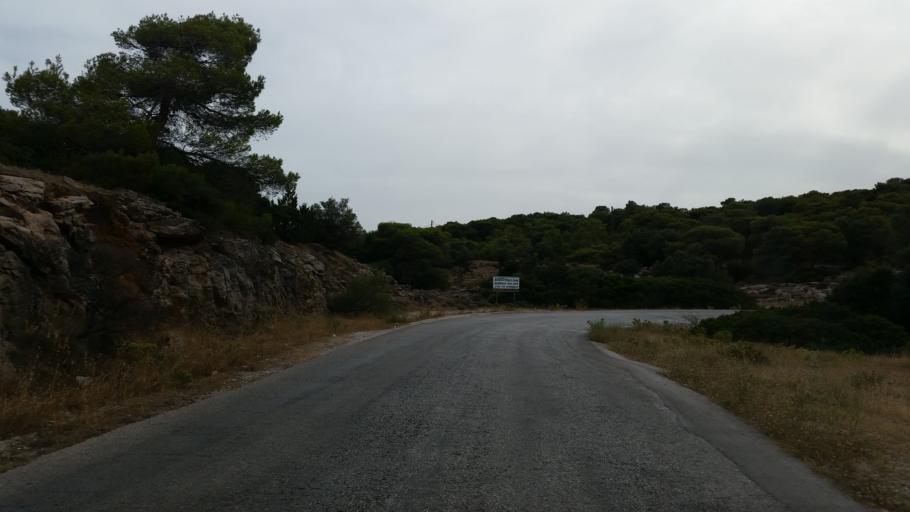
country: GR
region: Attica
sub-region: Nomarchia Anatolikis Attikis
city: Lavrio
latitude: 37.7186
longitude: 24.0339
